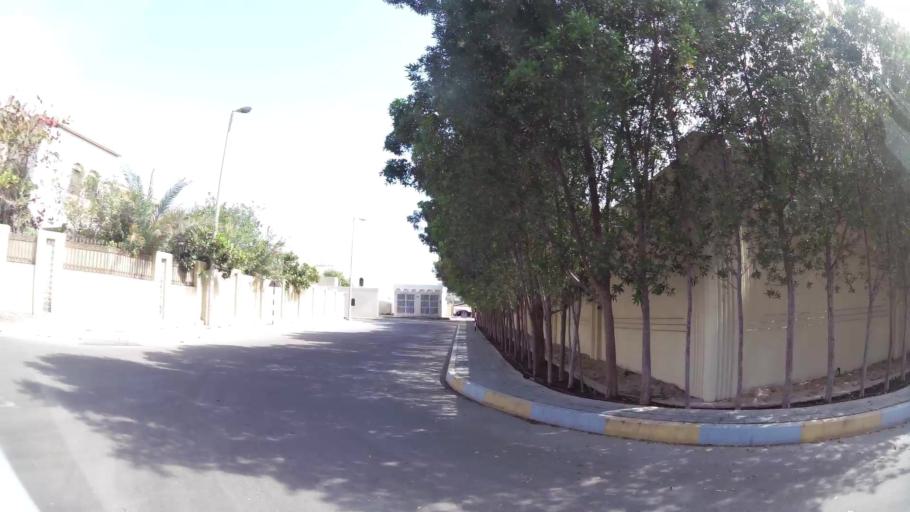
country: AE
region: Abu Dhabi
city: Abu Dhabi
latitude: 24.4424
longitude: 54.3610
